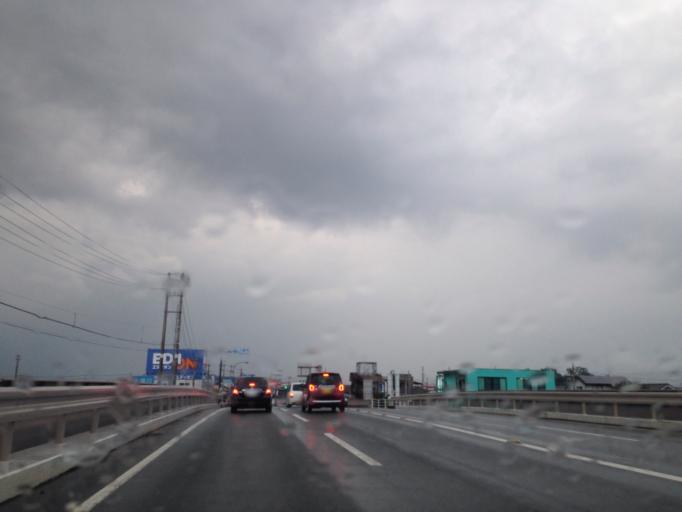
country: JP
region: Shizuoka
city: Mishima
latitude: 35.0834
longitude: 138.9322
